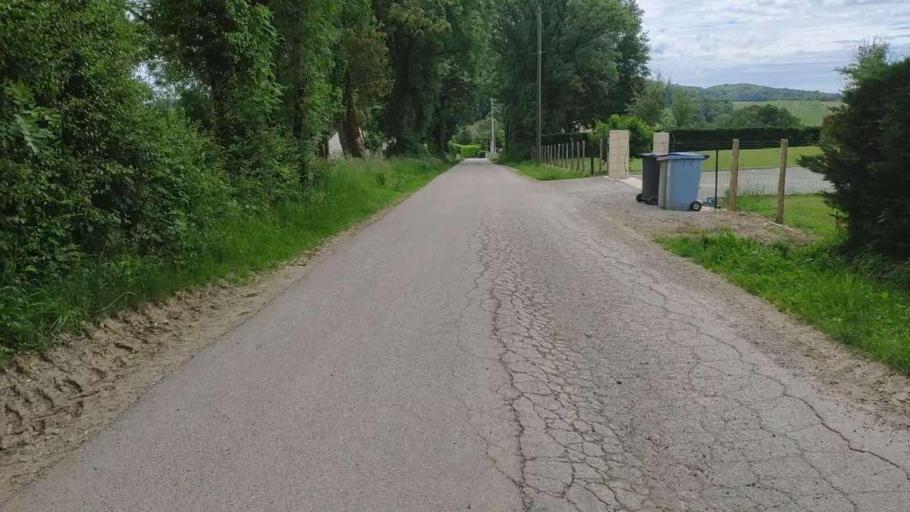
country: FR
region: Franche-Comte
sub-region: Departement du Jura
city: Montmorot
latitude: 46.7462
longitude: 5.5482
